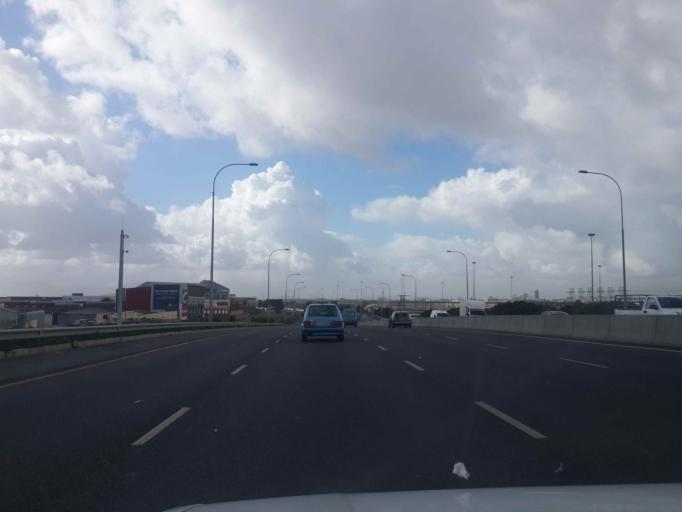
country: ZA
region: Western Cape
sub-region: City of Cape Town
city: Rosebank
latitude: -33.9209
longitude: 18.4621
